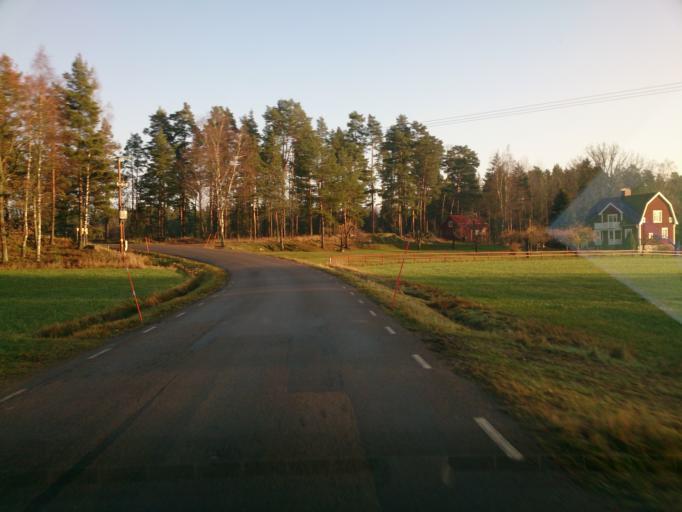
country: SE
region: OEstergoetland
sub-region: Atvidabergs Kommun
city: Atvidaberg
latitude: 58.3051
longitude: 15.9263
